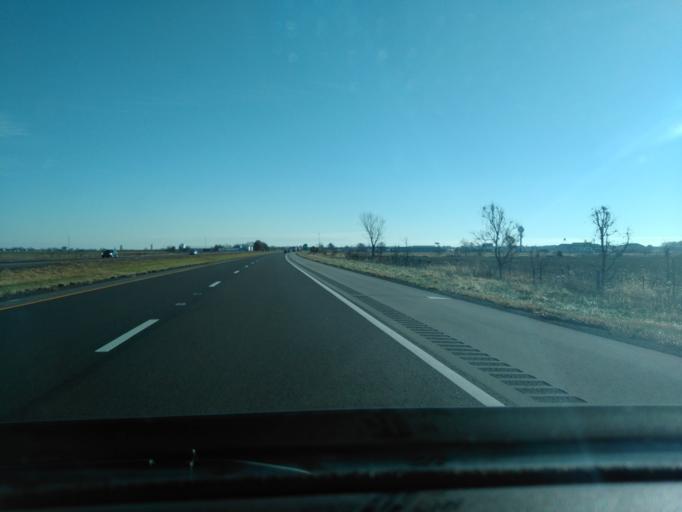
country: US
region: Illinois
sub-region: Madison County
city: Highland
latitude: 38.7864
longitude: -89.6446
